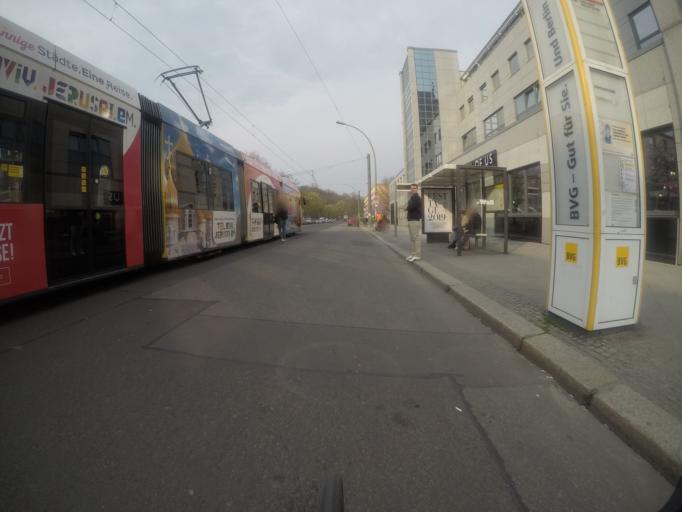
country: DE
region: Berlin
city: Fennpfuhl
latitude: 52.5303
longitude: 13.4614
